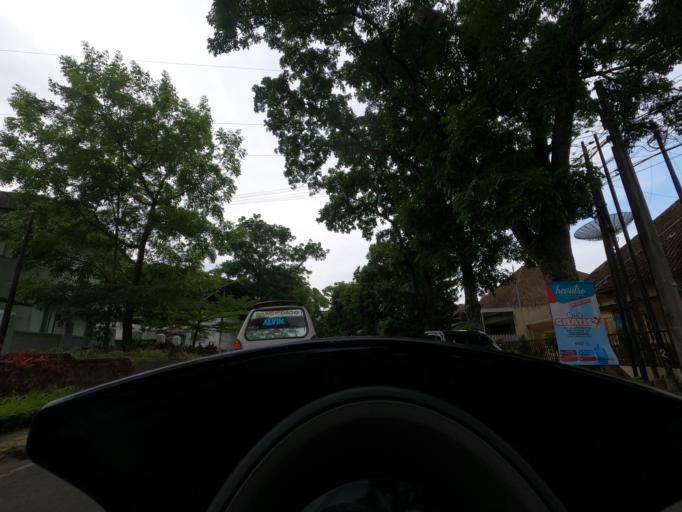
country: ID
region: West Java
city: Bandung
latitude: -6.9109
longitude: 107.6176
